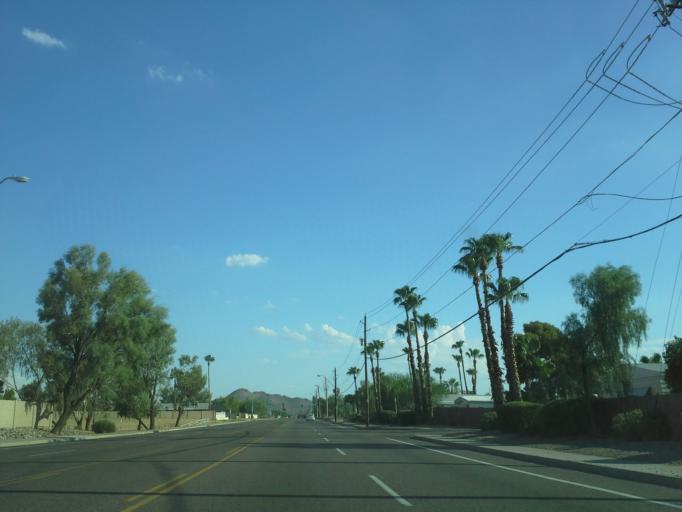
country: US
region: Arizona
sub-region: Maricopa County
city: Paradise Valley
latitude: 33.6511
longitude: -112.0309
